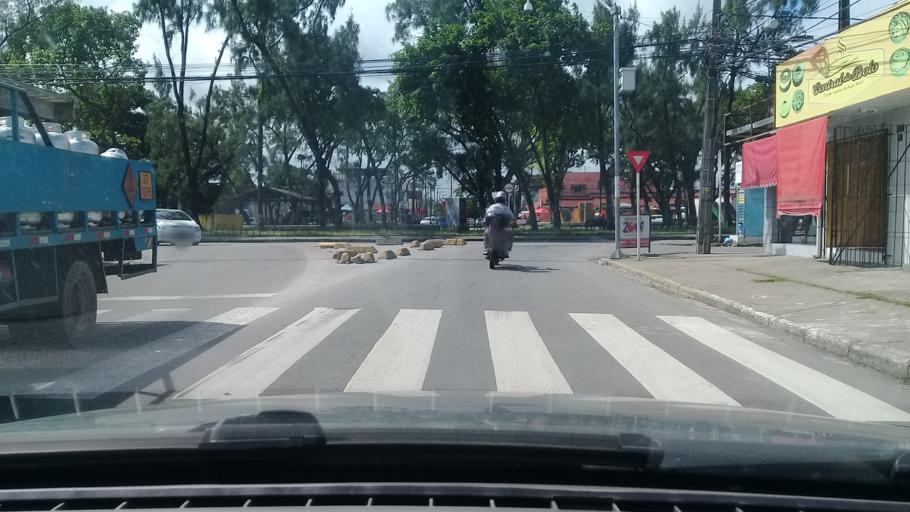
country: BR
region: Pernambuco
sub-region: Recife
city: Recife
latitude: -8.0716
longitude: -34.9290
